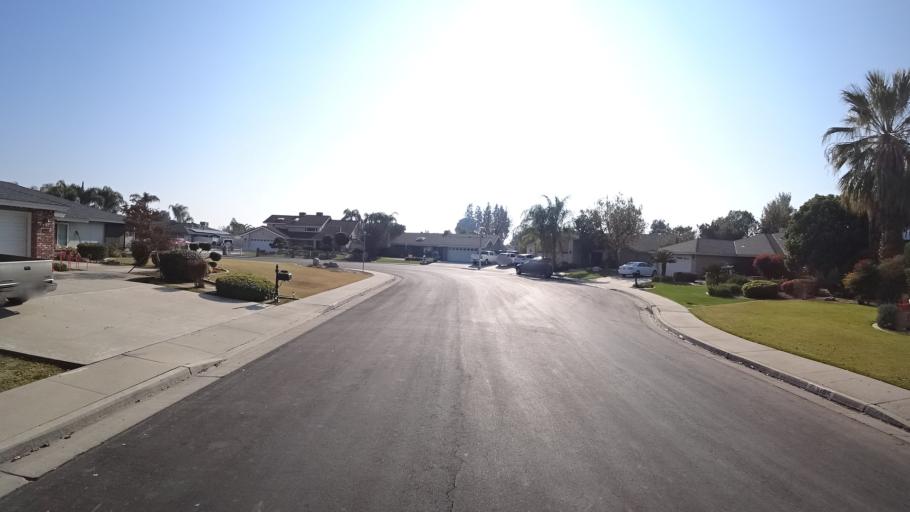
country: US
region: California
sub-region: Kern County
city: Greenacres
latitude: 35.3267
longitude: -119.0832
